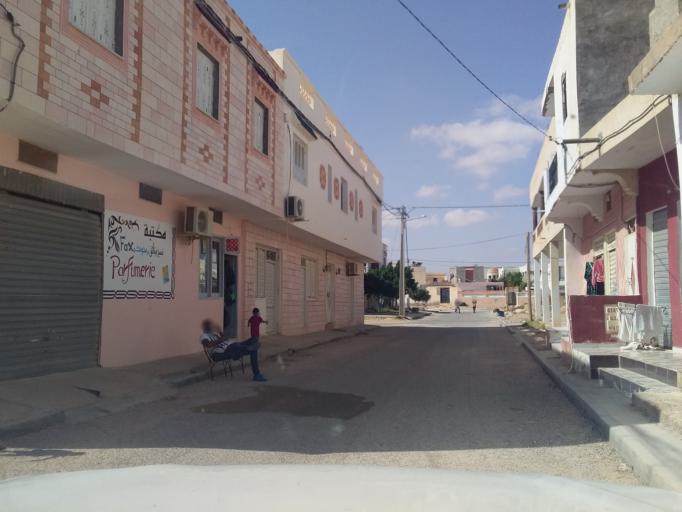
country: TN
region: Madanin
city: Medenine
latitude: 33.5838
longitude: 10.3228
